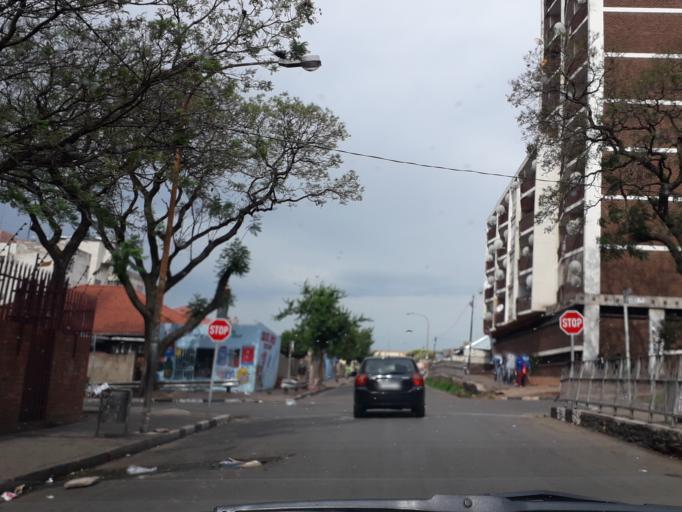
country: ZA
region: Gauteng
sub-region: City of Johannesburg Metropolitan Municipality
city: Johannesburg
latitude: -26.1859
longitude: 28.0554
